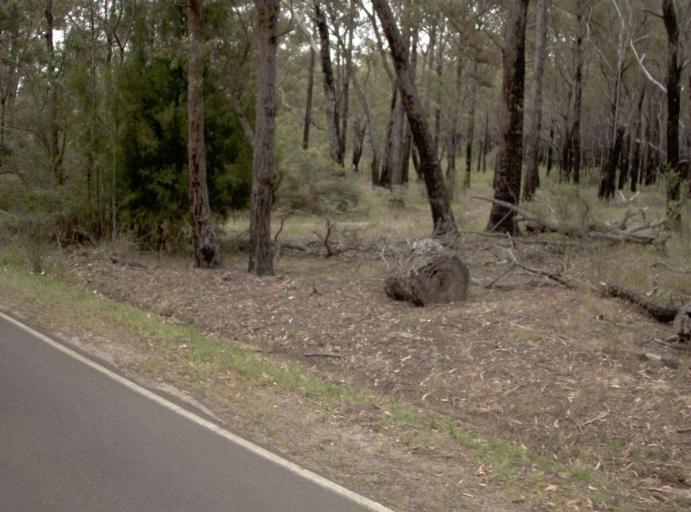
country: AU
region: Victoria
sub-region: Latrobe
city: Traralgon
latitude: -38.4762
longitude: 146.8219
